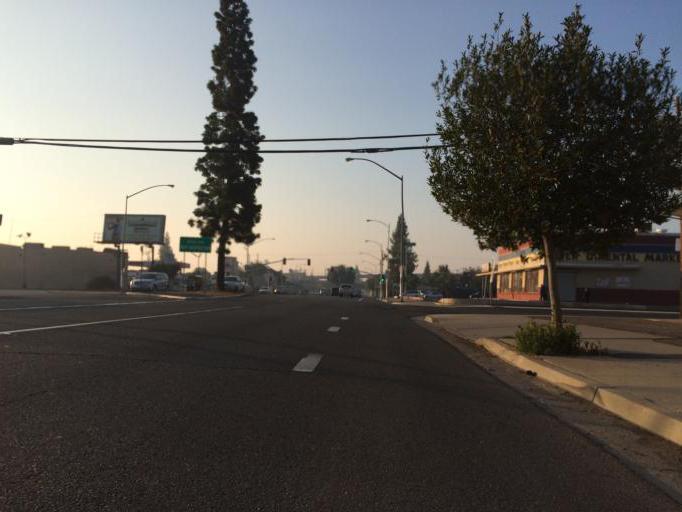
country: US
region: California
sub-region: Fresno County
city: Fresno
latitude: 36.7590
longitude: -119.7726
